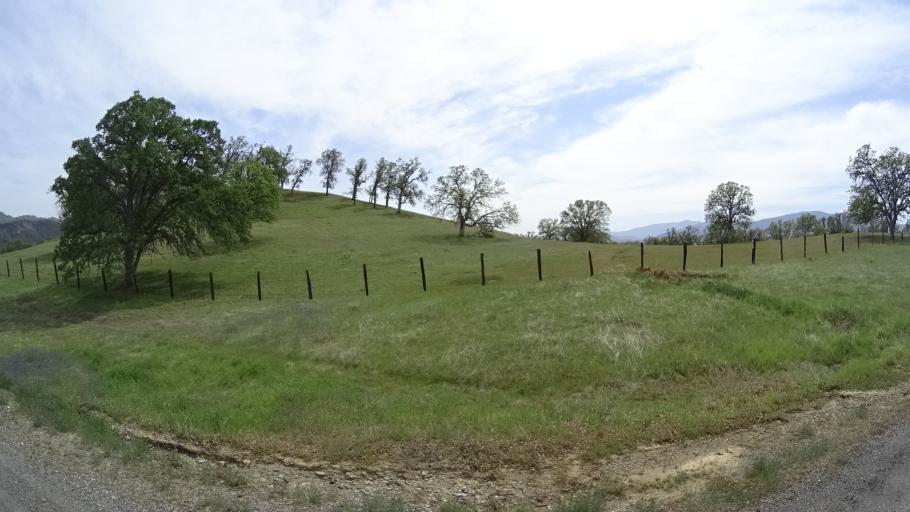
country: US
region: California
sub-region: Glenn County
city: Willows
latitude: 39.6062
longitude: -122.5546
